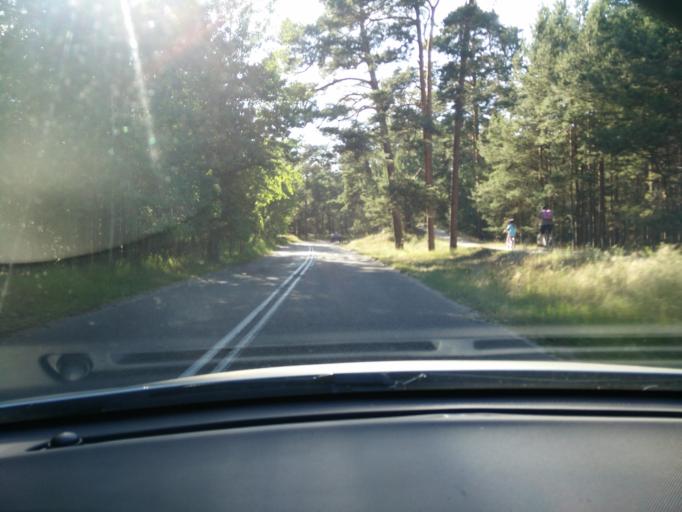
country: PL
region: Pomeranian Voivodeship
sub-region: Powiat pucki
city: Hel
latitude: 54.6490
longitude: 18.7651
